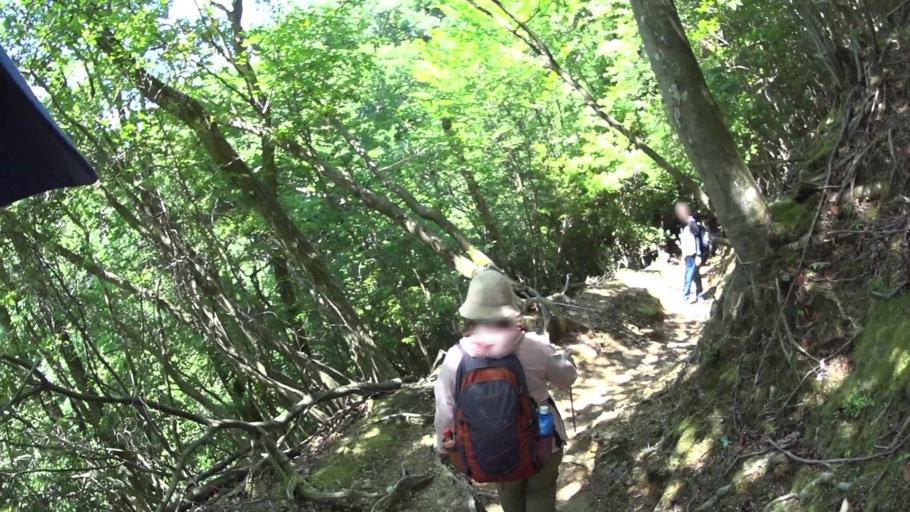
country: JP
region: Kyoto
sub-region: Kyoto-shi
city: Kamigyo-ku
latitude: 35.0551
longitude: 135.8148
